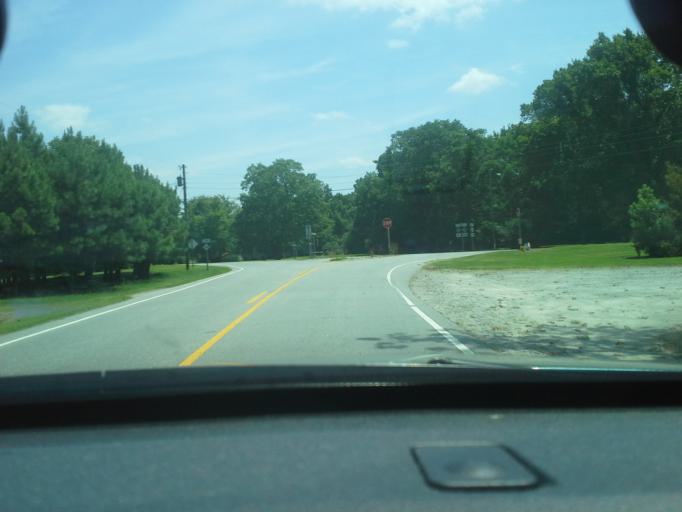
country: US
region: North Carolina
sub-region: Chowan County
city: Edenton
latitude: 35.9251
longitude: -76.5913
